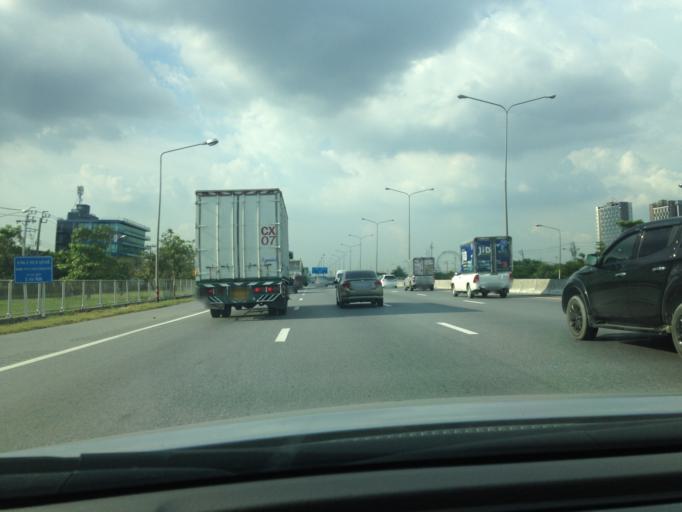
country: TH
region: Bangkok
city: Khan Na Yao
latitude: 13.8104
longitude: 100.6779
